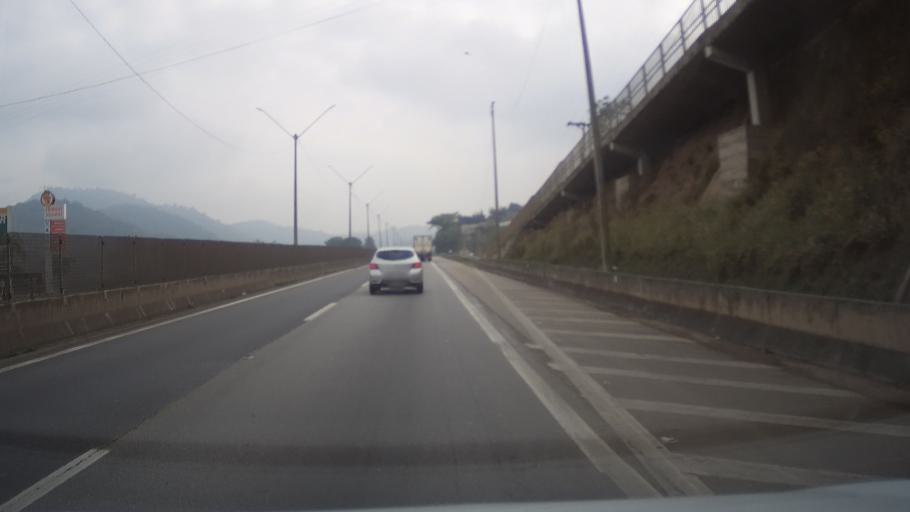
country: BR
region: Sao Paulo
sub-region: Atibaia
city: Atibaia
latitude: -23.0429
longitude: -46.5600
